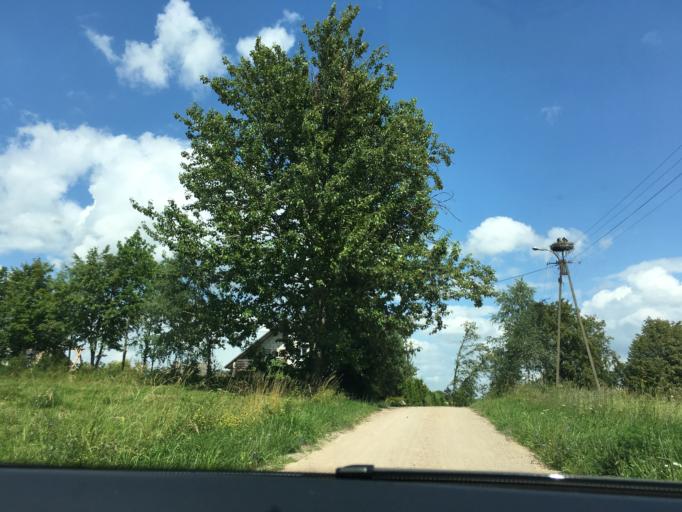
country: PL
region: Podlasie
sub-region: Powiat sejnenski
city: Krasnopol
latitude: 54.0919
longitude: 23.2652
